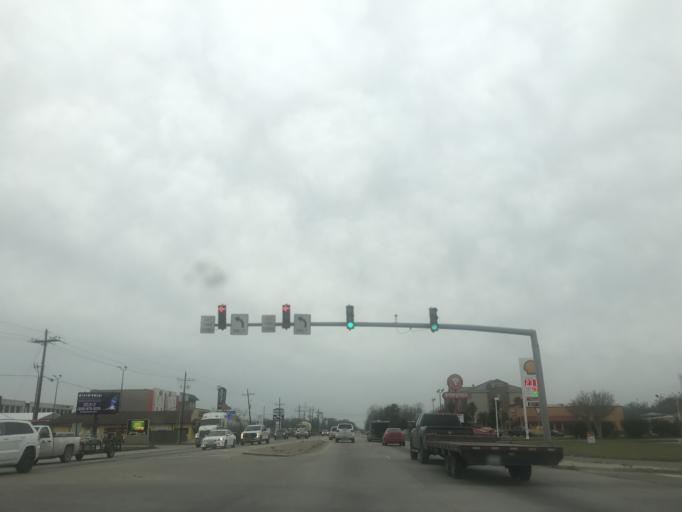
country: US
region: Louisiana
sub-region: Ascension Parish
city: Gonzales
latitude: 30.2107
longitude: -90.9505
